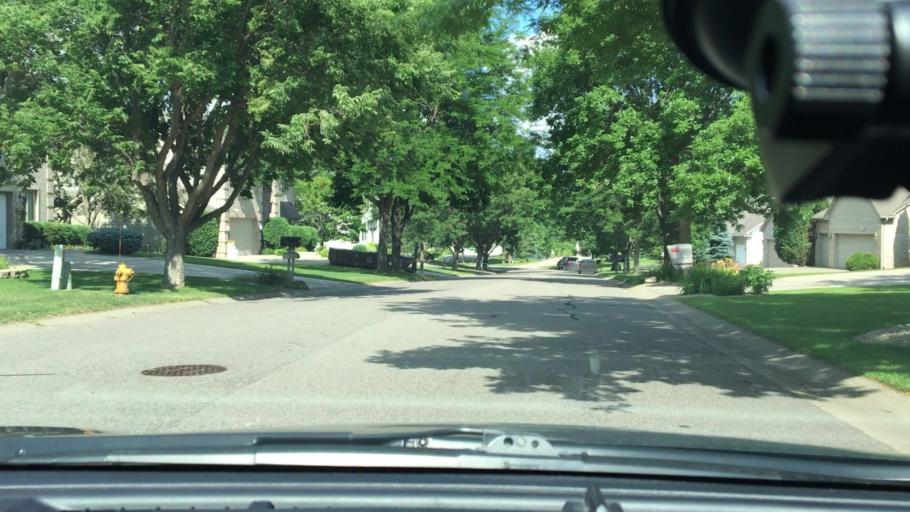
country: US
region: Minnesota
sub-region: Hennepin County
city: Plymouth
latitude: 45.0322
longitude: -93.4390
